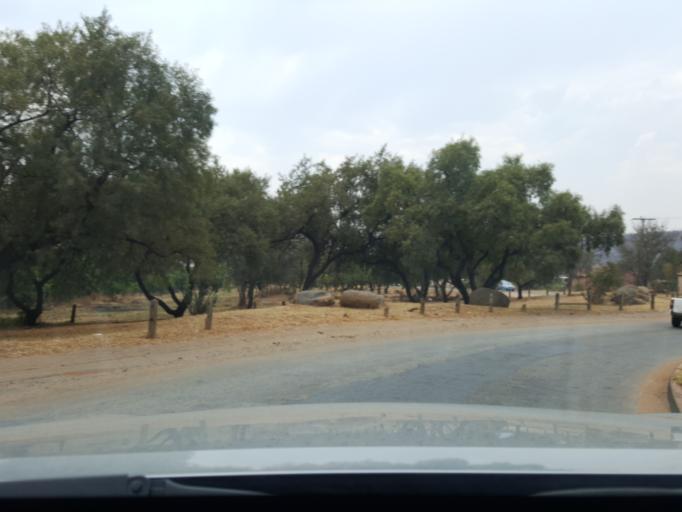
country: ZA
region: North-West
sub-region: Ngaka Modiri Molema District Municipality
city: Zeerust
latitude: -25.4994
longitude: 25.9838
